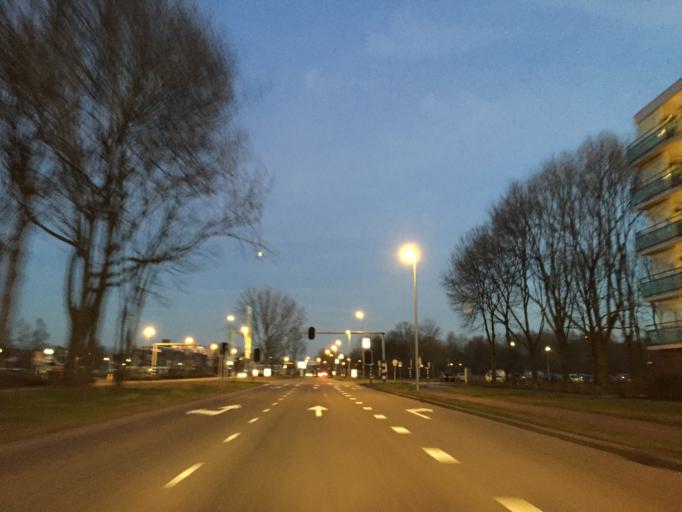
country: NL
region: South Holland
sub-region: Gemeente Leiderdorp
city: Leiderdorp
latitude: 52.1622
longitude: 4.5307
